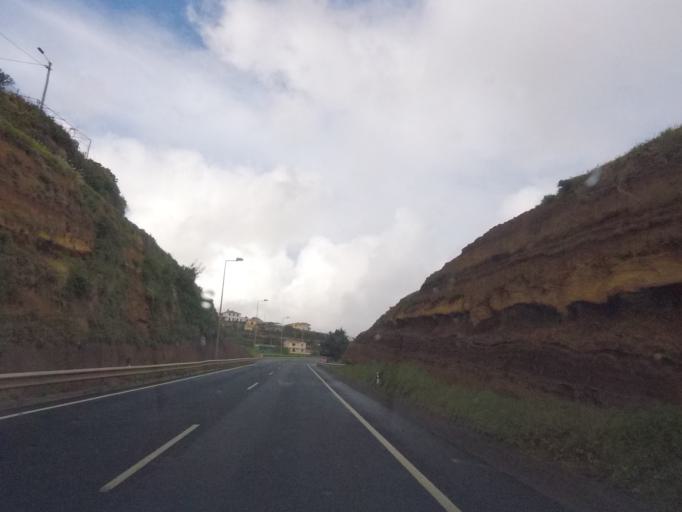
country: PT
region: Madeira
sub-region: Santa Cruz
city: Santa Cruz
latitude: 32.6747
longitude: -16.8021
